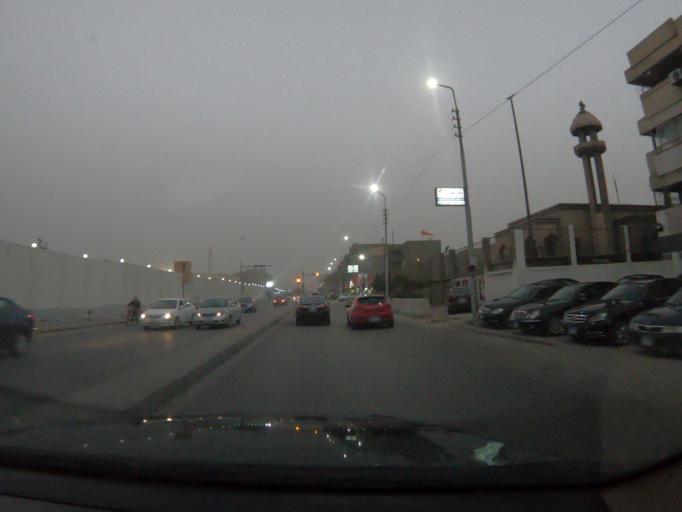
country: EG
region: Muhafazat al Qahirah
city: Cairo
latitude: 30.0860
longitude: 31.3529
